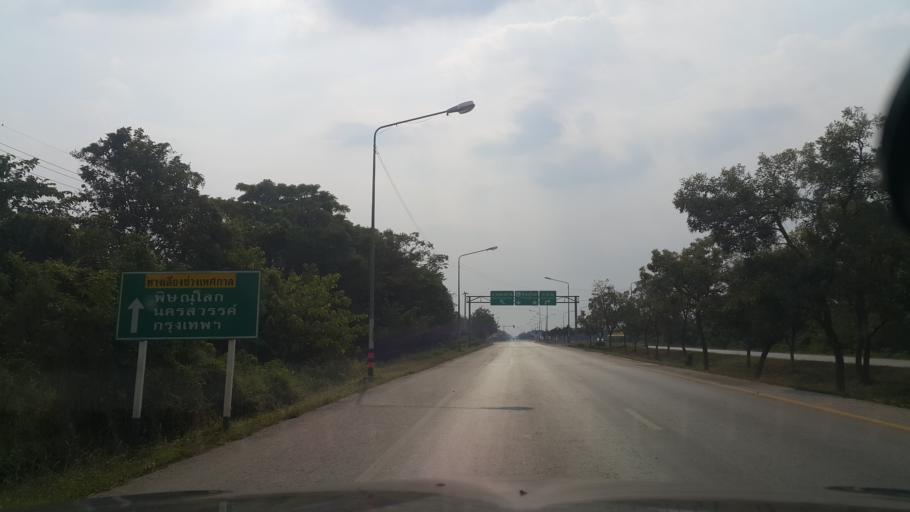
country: TH
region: Sukhothai
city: Sukhothai
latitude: 17.0549
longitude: 99.9006
